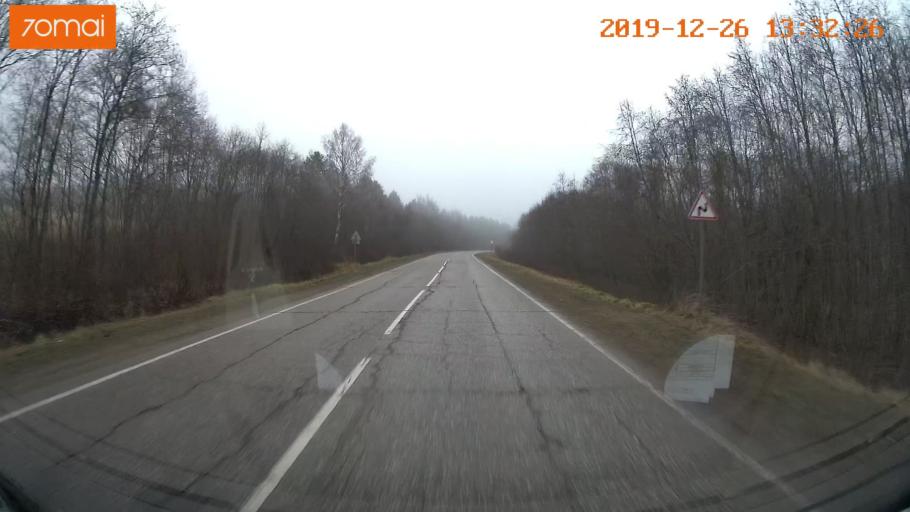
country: RU
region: Vologda
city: Sheksna
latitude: 58.8290
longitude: 38.2906
